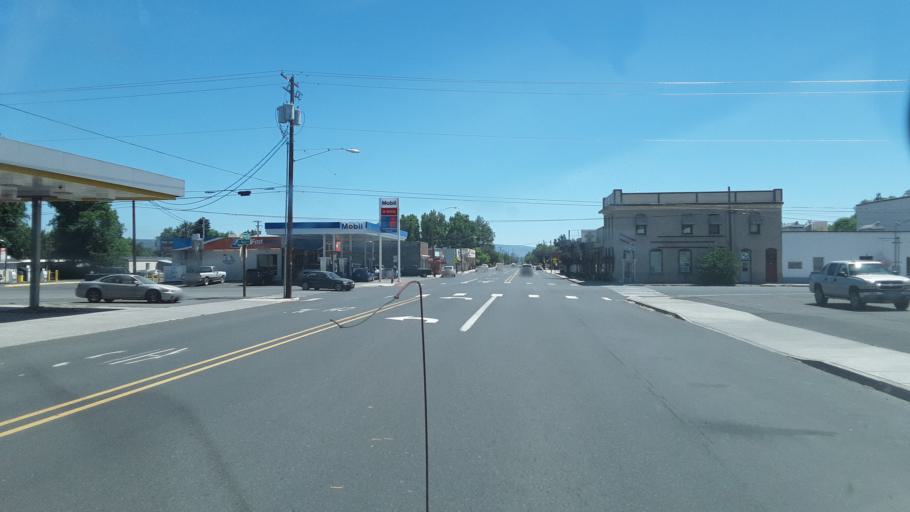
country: US
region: California
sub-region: Siskiyou County
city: Tulelake
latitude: 42.0240
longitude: -121.6010
